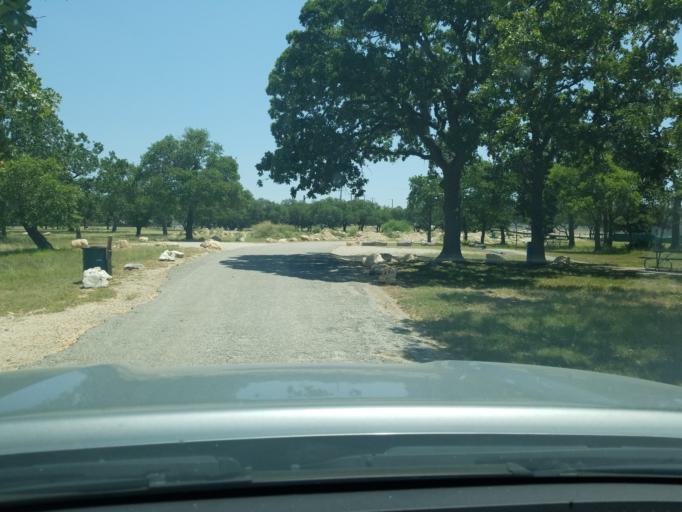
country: US
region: Texas
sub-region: Bexar County
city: Timberwood Park
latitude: 29.7081
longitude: -98.5149
